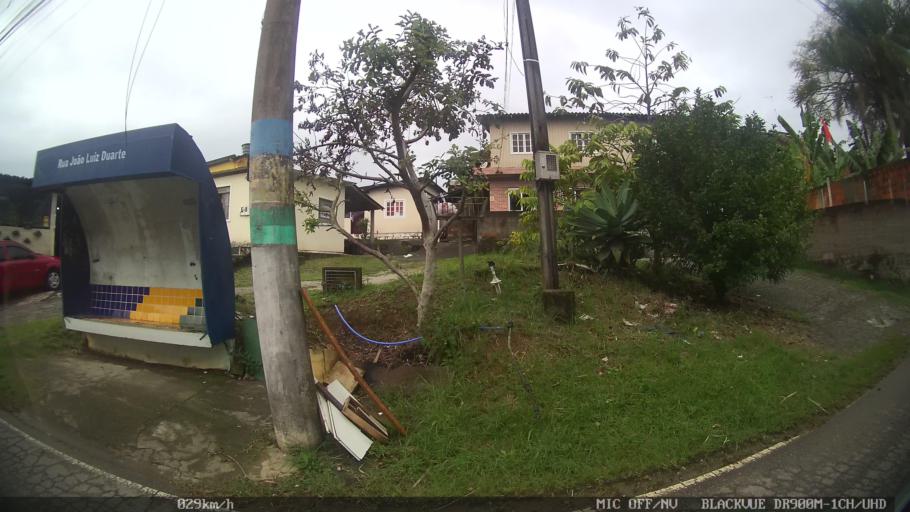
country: BR
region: Santa Catarina
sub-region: Biguacu
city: Biguacu
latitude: -27.5328
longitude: -48.6385
